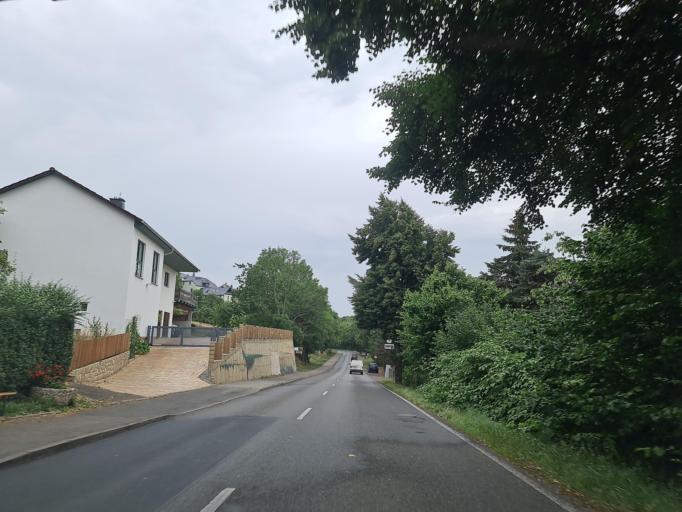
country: DE
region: Saxony
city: Augustusburg
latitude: 50.8133
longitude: 13.1027
